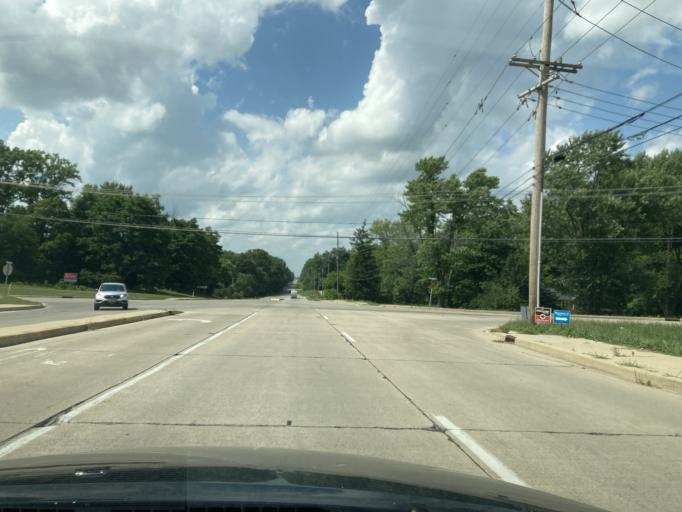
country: US
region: Indiana
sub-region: Boone County
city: Zionsville
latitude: 39.9620
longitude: -86.2470
